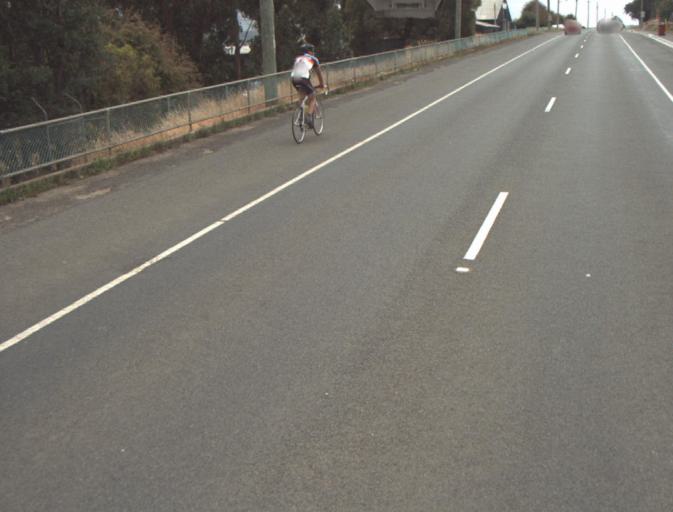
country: AU
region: Tasmania
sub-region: Launceston
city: Newstead
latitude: -41.4450
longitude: 147.1838
